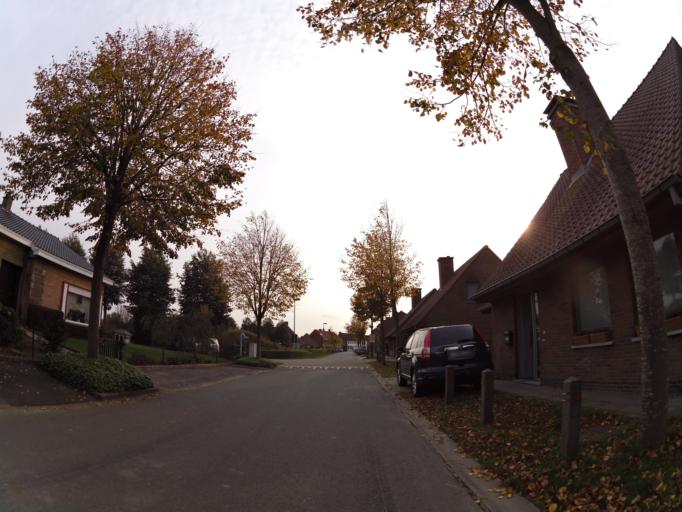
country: BE
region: Flanders
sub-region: Provincie West-Vlaanderen
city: Jabbeke
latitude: 51.2165
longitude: 3.0735
